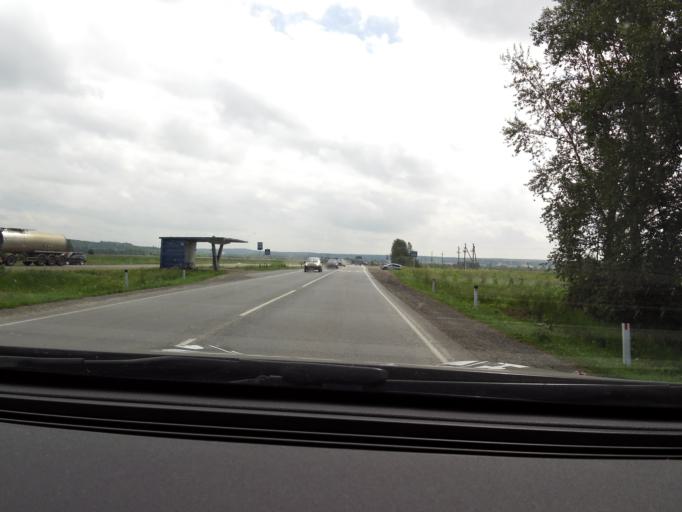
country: RU
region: Perm
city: Kukushtan
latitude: 57.5147
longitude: 56.6402
